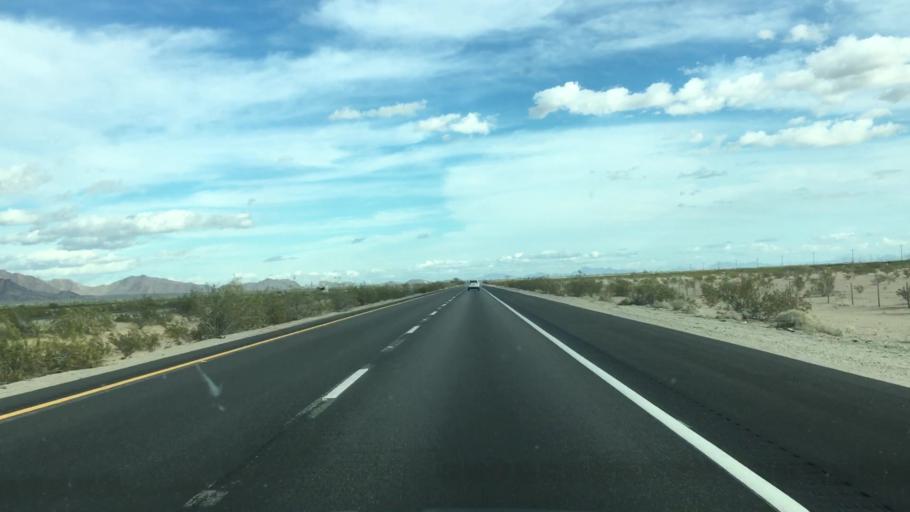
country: US
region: California
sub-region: Riverside County
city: Mesa Verde
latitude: 33.6079
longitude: -114.8930
